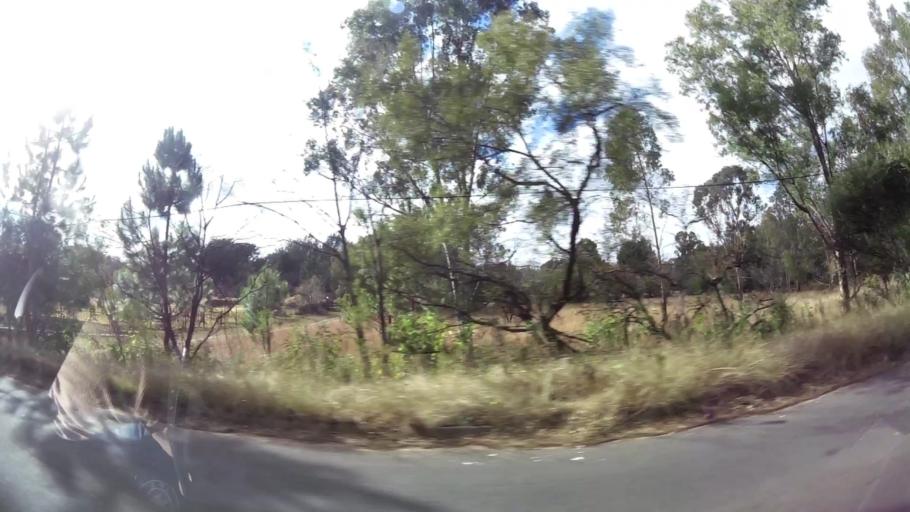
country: ZA
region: Gauteng
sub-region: West Rand District Municipality
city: Muldersdriseloop
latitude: -26.0881
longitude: 27.8533
